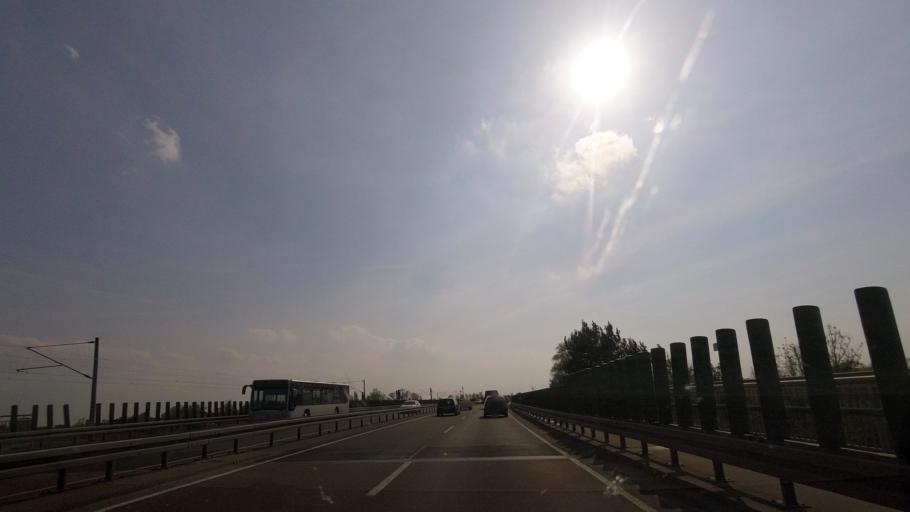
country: DE
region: Saxony-Anhalt
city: Wittenburg
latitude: 51.8489
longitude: 12.6465
